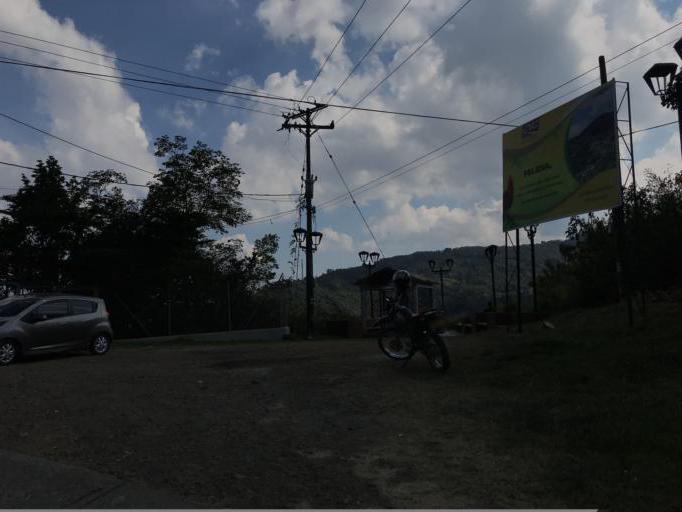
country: CO
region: Valle del Cauca
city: Cali
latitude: 3.4677
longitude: -76.6260
